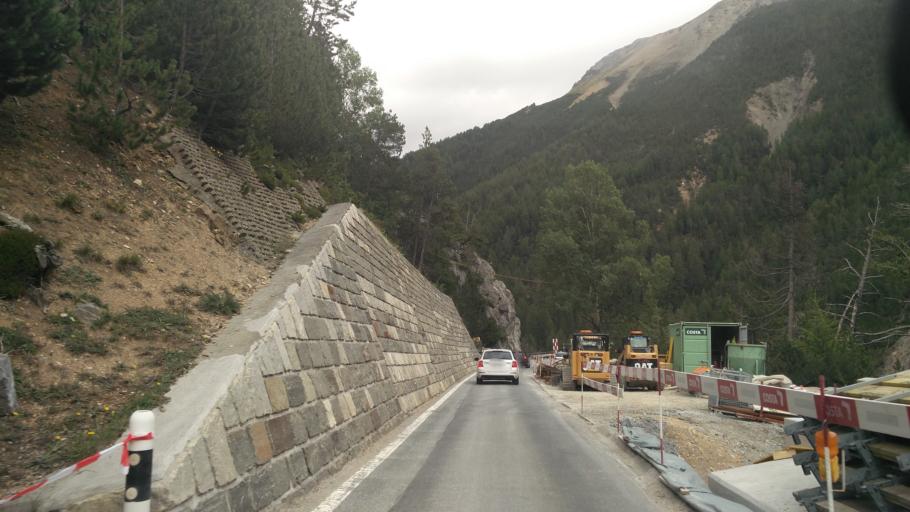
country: CH
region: Grisons
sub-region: Inn District
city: Zernez
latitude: 46.6532
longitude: 10.1823
